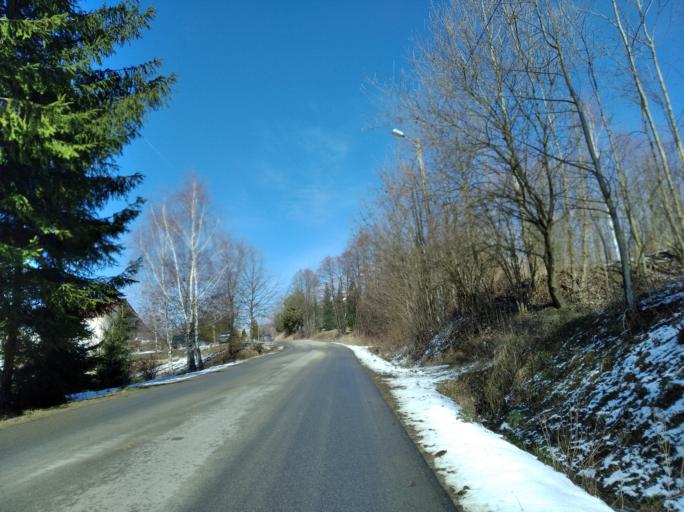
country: PL
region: Subcarpathian Voivodeship
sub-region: Powiat brzozowski
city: Jablonica Polska
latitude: 49.7199
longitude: 21.8802
